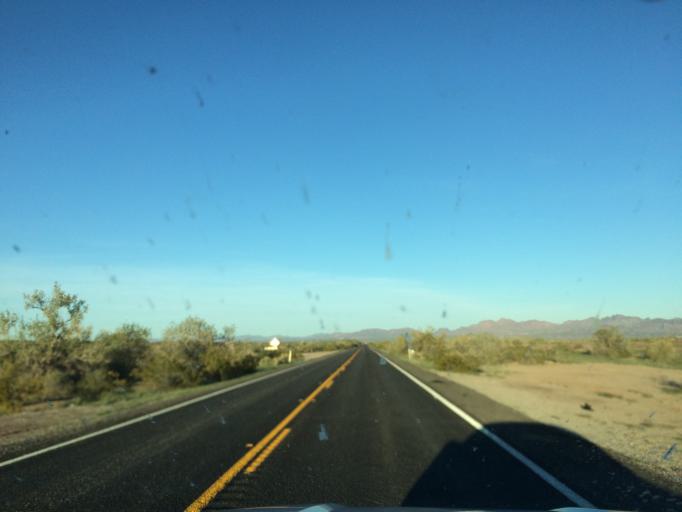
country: US
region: California
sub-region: Riverside County
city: Mesa Verde
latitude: 33.2836
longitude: -114.7762
